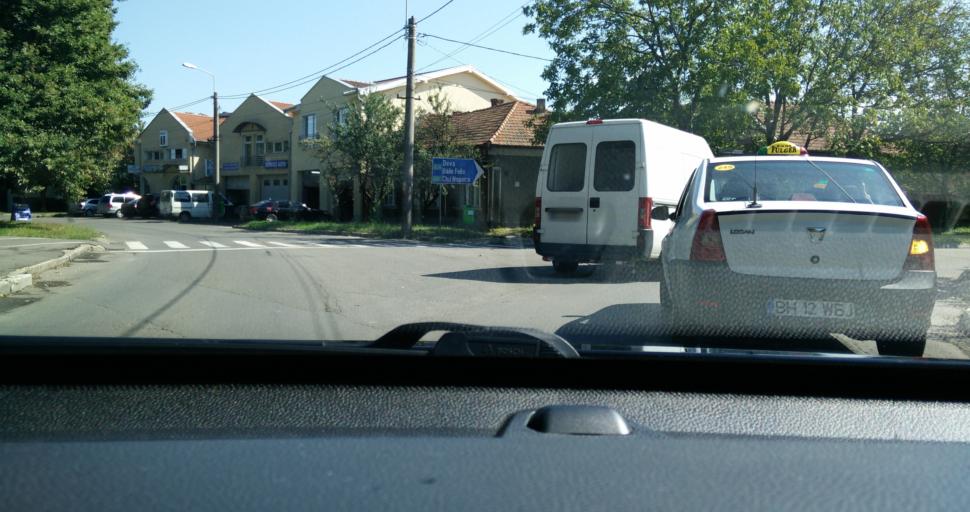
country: RO
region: Bihor
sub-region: Comuna Biharea
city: Oradea
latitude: 47.0430
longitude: 21.9354
